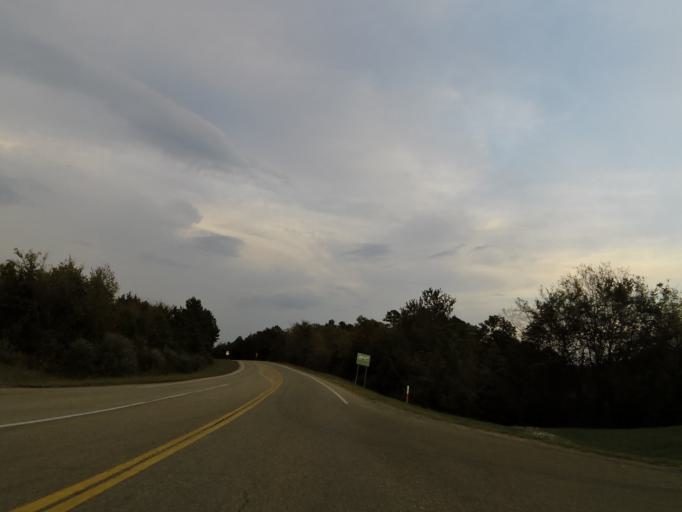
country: US
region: Tennessee
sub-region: Monroe County
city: Vonore
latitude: 35.6612
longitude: -84.2854
